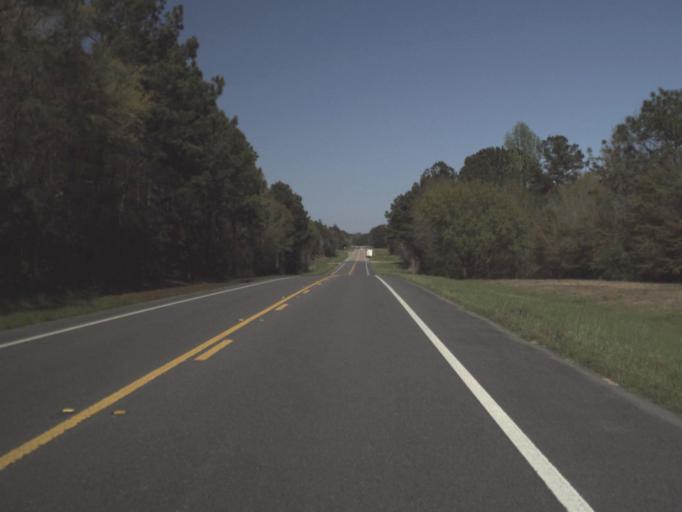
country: US
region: Florida
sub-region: Walton County
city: DeFuniak Springs
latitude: 30.7351
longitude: -85.9153
